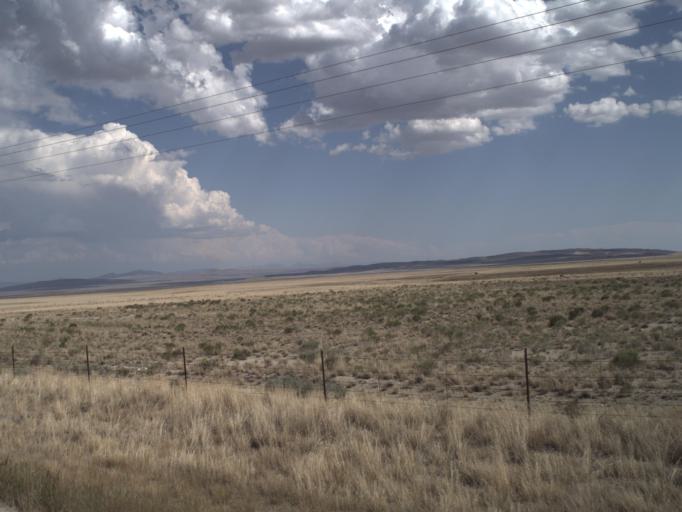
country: US
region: Idaho
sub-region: Minidoka County
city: Rupert
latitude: 41.9698
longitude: -113.1183
